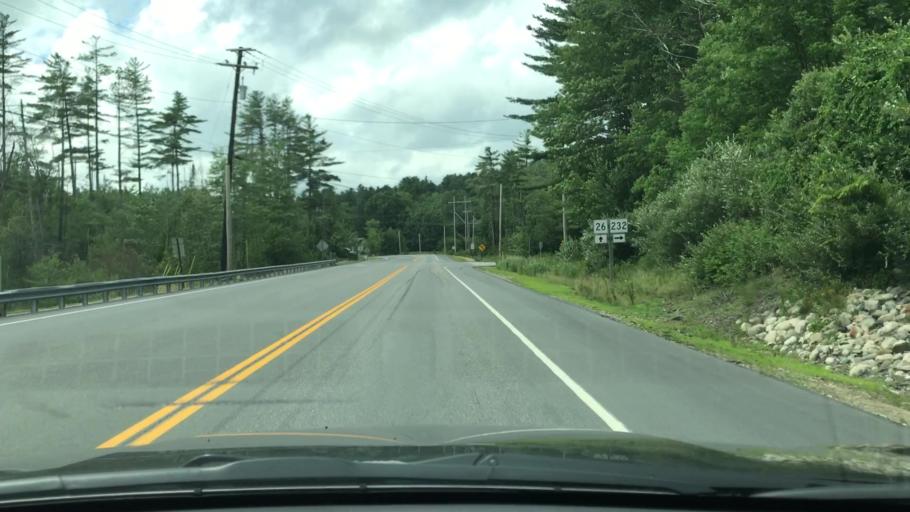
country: US
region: Maine
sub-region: Oxford County
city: West Paris
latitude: 44.3858
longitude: -70.6284
